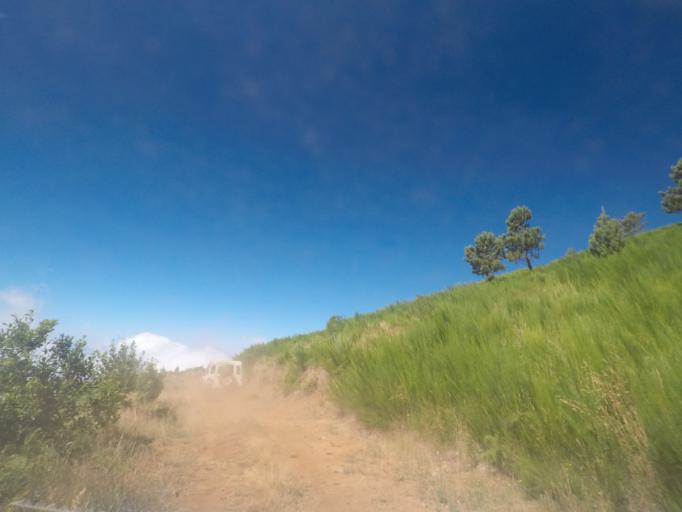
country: PT
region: Madeira
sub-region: Funchal
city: Nossa Senhora do Monte
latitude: 32.7065
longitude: -16.9115
